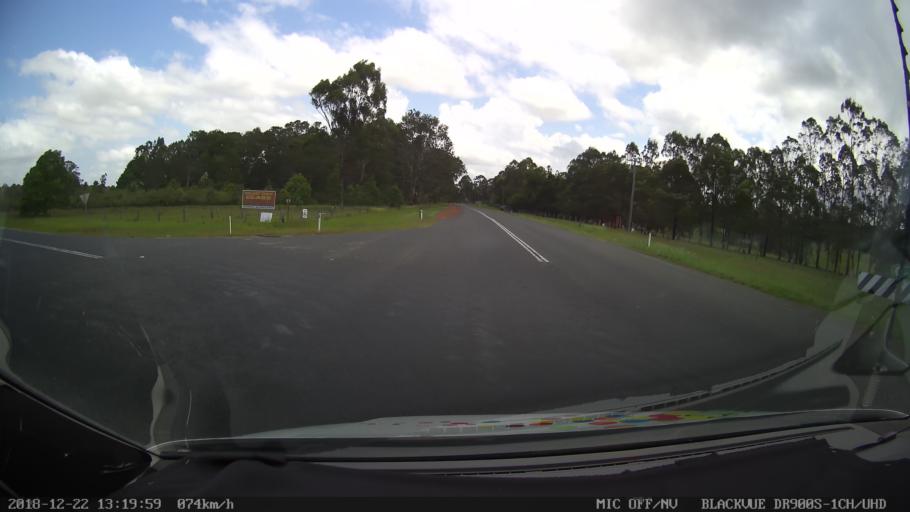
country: AU
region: New South Wales
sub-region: Clarence Valley
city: South Grafton
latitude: -29.7617
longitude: 152.9301
